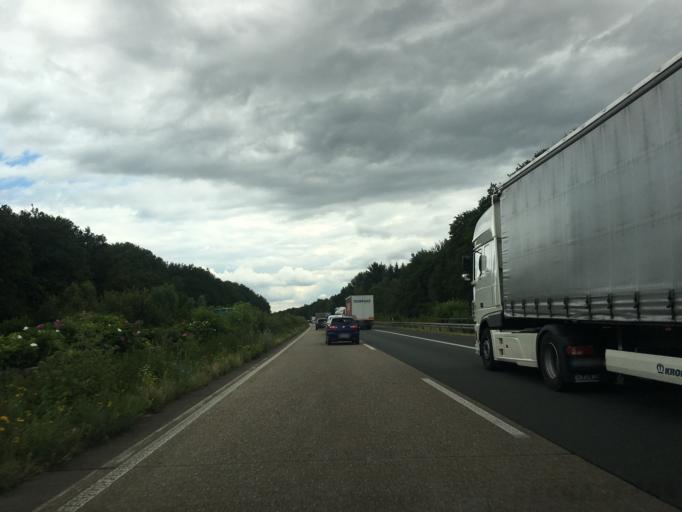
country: DE
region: North Rhine-Westphalia
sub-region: Regierungsbezirk Munster
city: Senden
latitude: 51.8604
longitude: 7.5765
